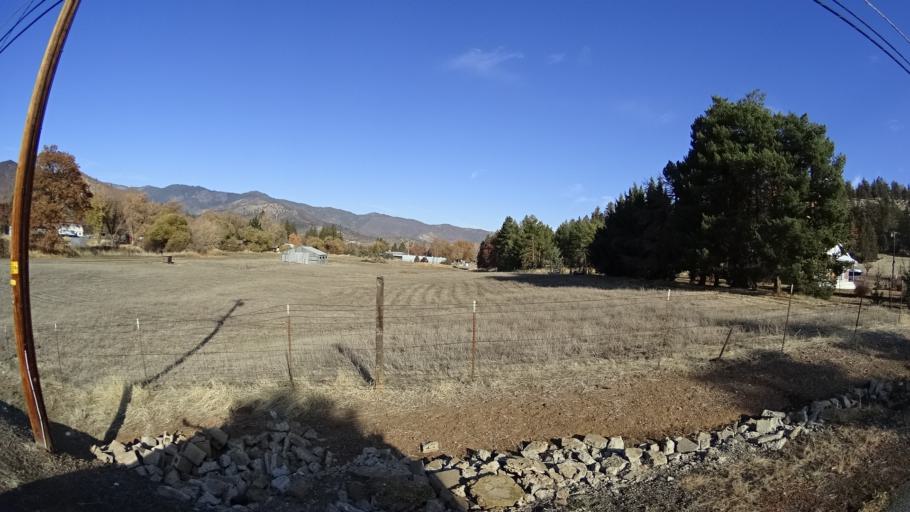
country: US
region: California
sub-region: Siskiyou County
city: Yreka
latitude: 41.6998
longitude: -122.6381
